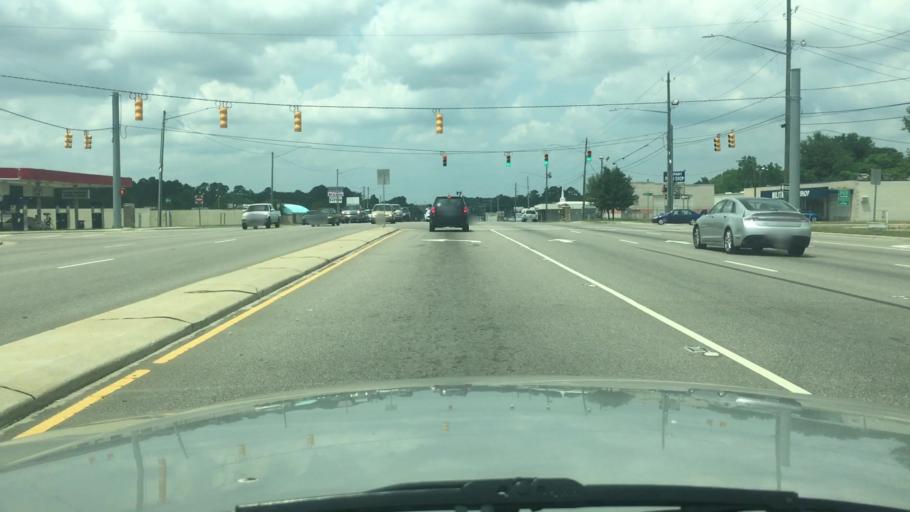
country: US
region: North Carolina
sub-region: Cumberland County
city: Fort Bragg
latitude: 35.0926
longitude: -78.9549
